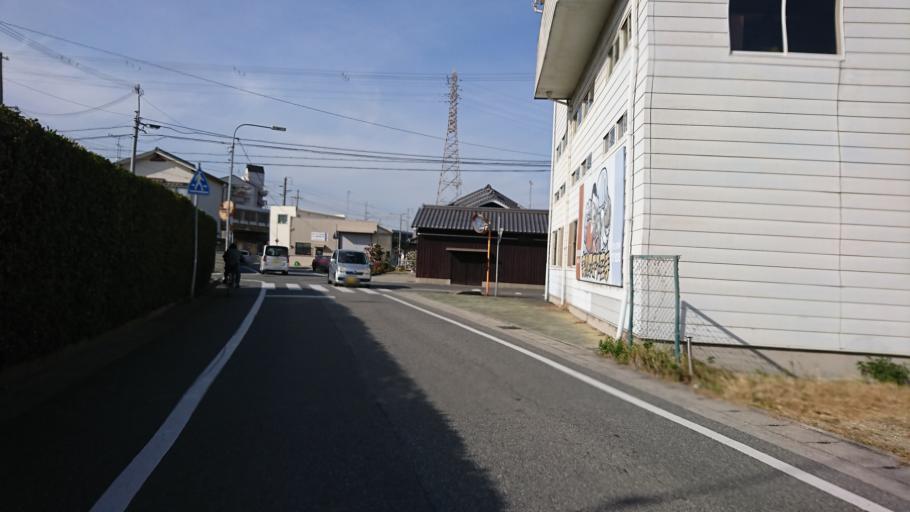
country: JP
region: Hyogo
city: Kakogawacho-honmachi
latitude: 34.7294
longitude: 134.8539
